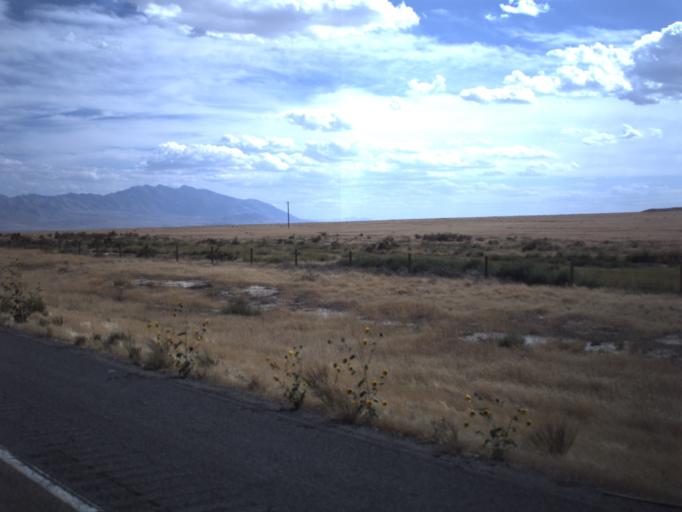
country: US
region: Utah
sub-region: Tooele County
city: Grantsville
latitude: 40.8017
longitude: -112.8528
